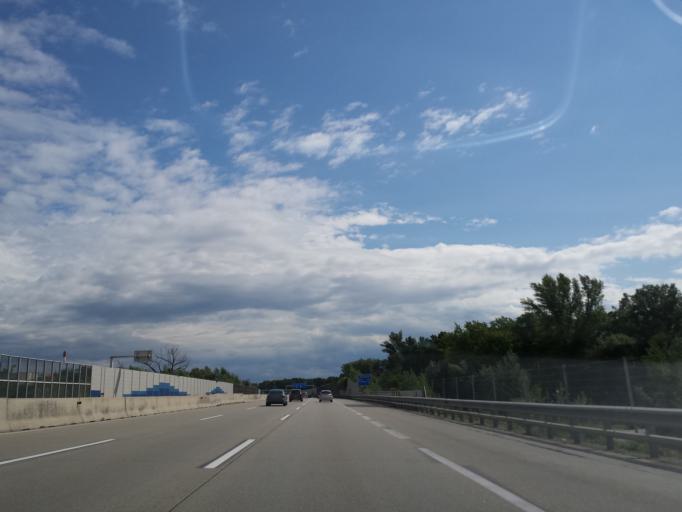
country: AT
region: Lower Austria
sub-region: Politischer Bezirk Korneuburg
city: Korneuburg
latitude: 48.3465
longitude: 16.3201
